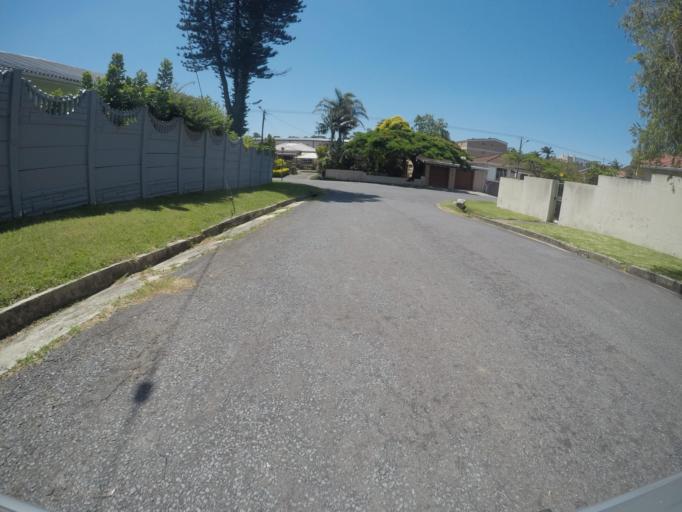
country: ZA
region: Eastern Cape
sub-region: Buffalo City Metropolitan Municipality
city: East London
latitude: -32.9859
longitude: 27.9065
